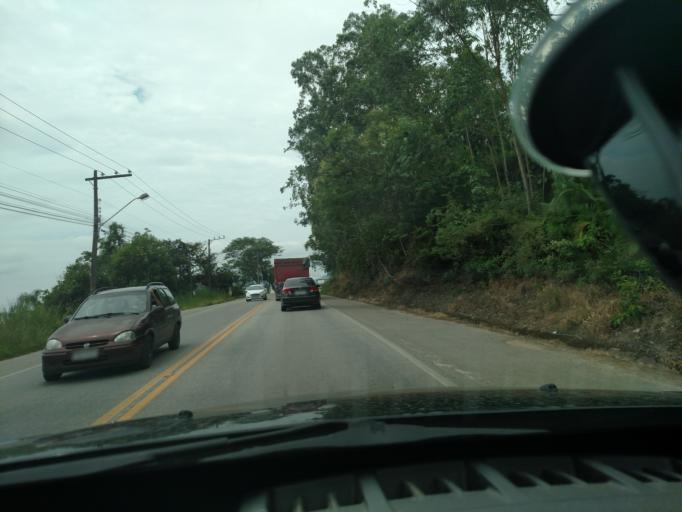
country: BR
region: Santa Catarina
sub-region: Itajai
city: Itajai
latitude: -26.8885
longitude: -48.7547
